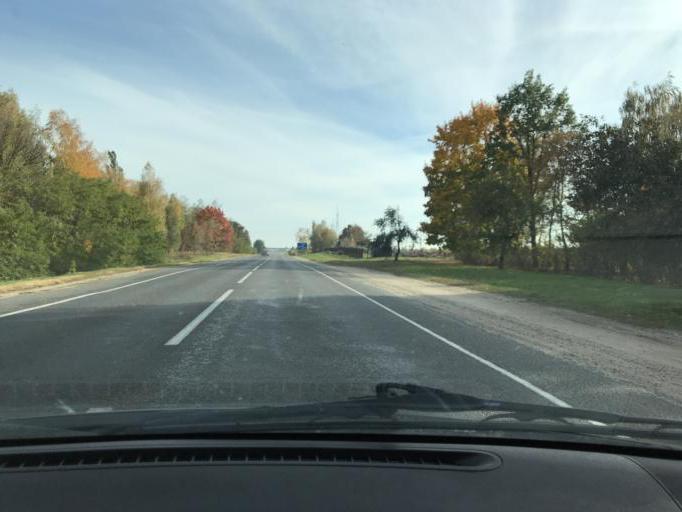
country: BY
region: Brest
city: Asnyezhytsy
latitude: 52.1928
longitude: 26.0723
